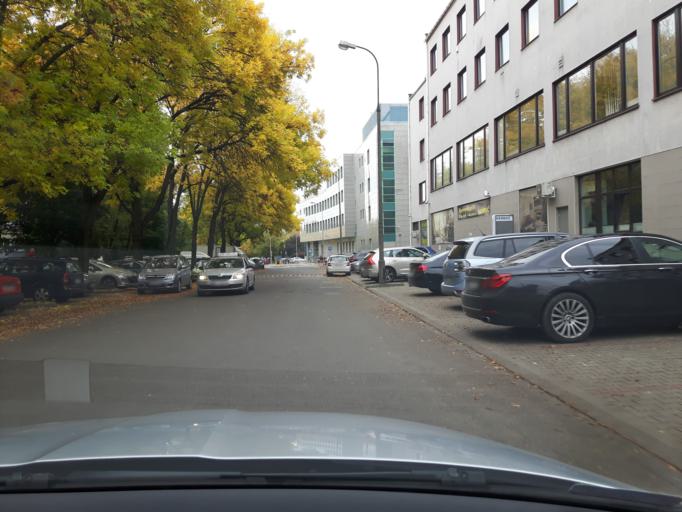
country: PL
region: Masovian Voivodeship
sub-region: Warszawa
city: Mokotow
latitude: 52.1749
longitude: 21.0036
